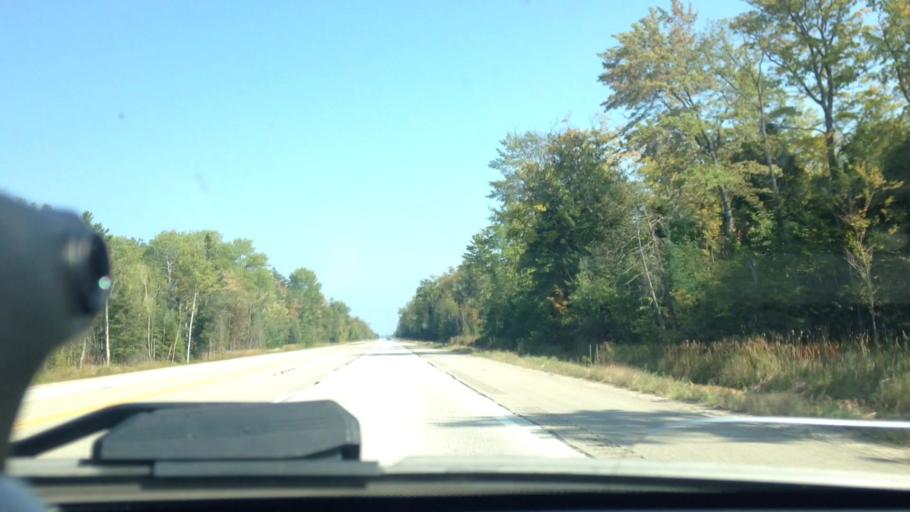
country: US
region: Michigan
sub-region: Luce County
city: Newberry
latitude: 46.3035
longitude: -85.2826
